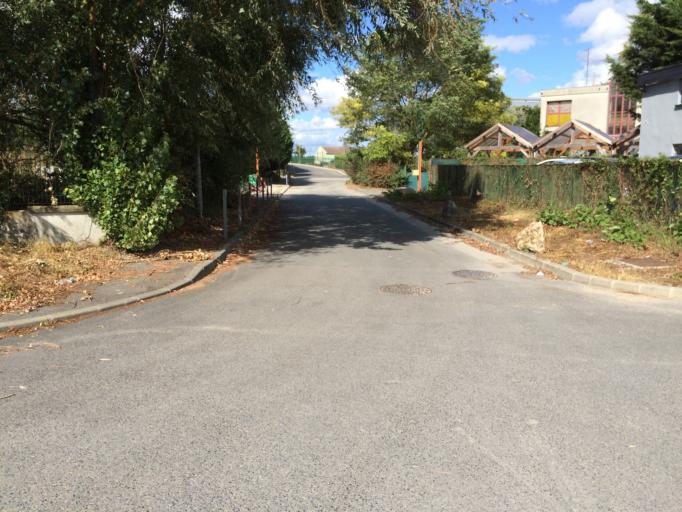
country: FR
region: Ile-de-France
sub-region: Departement de l'Essonne
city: Saulx-les-Chartreux
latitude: 48.6966
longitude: 2.2667
